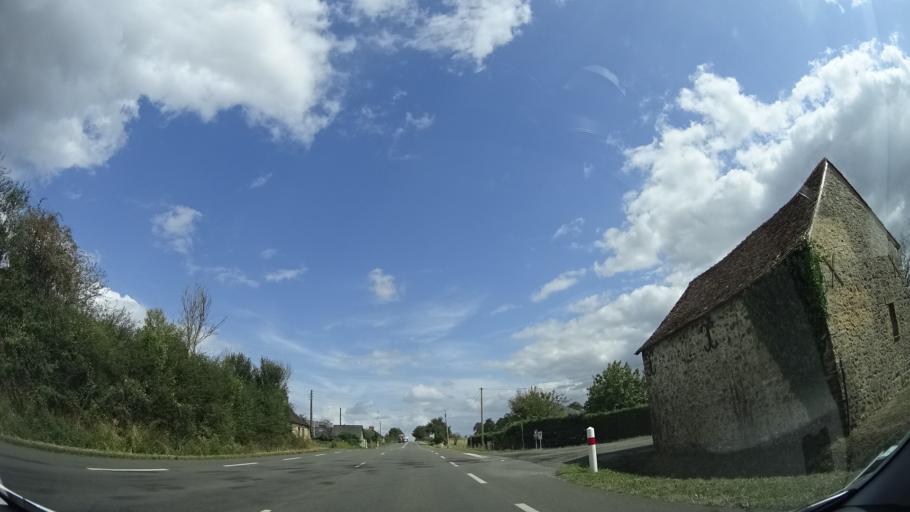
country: FR
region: Pays de la Loire
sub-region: Departement de la Mayenne
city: Sainte-Suzanne
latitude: 48.0338
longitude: -0.3699
